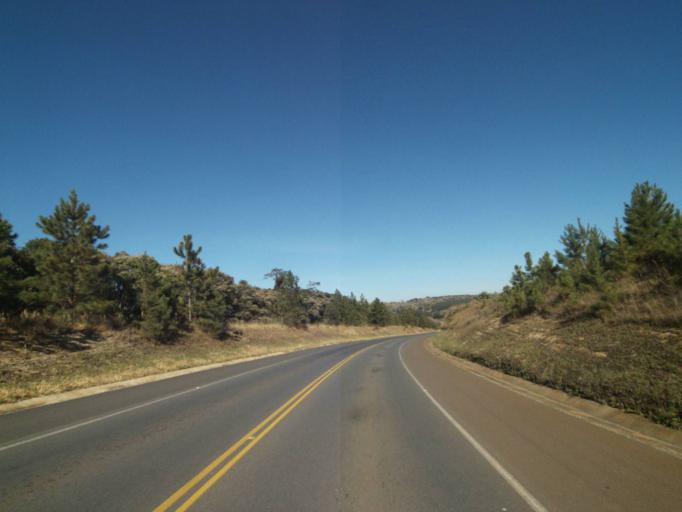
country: BR
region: Parana
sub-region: Tibagi
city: Tibagi
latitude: -24.3974
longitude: -50.3365
